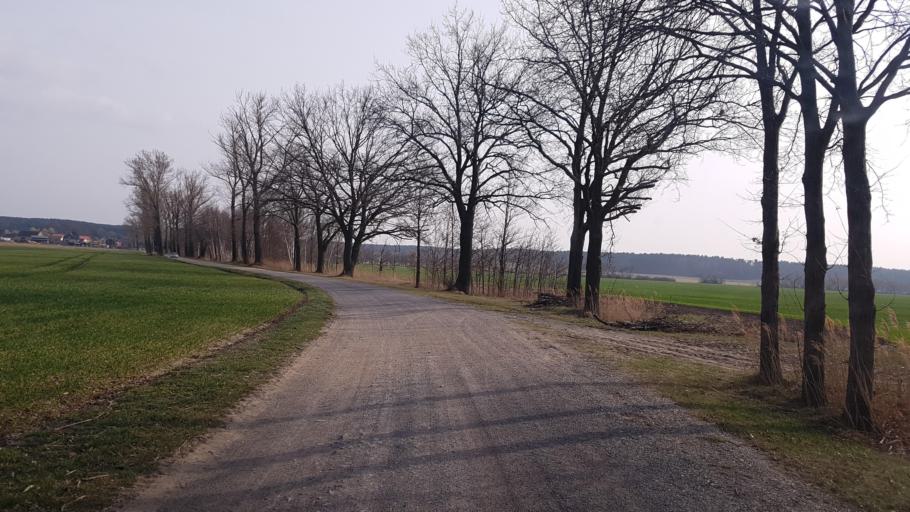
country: DE
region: Brandenburg
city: Merzdorf
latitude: 51.4126
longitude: 13.5267
